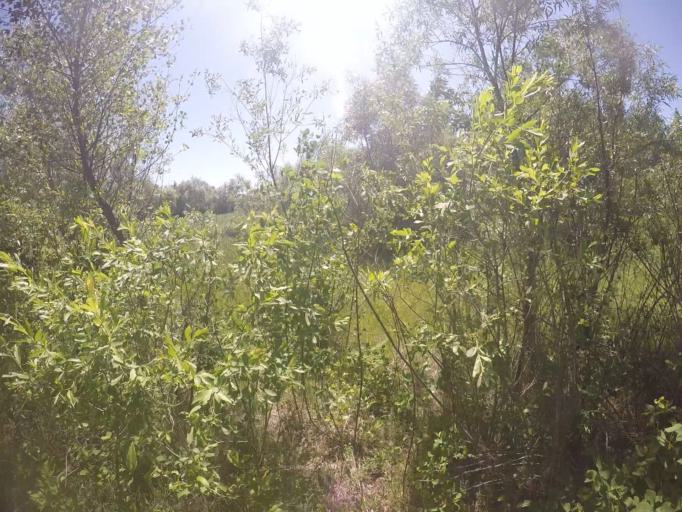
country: RU
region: Saratov
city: Krasnyy Oktyabr'
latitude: 51.3100
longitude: 45.5499
